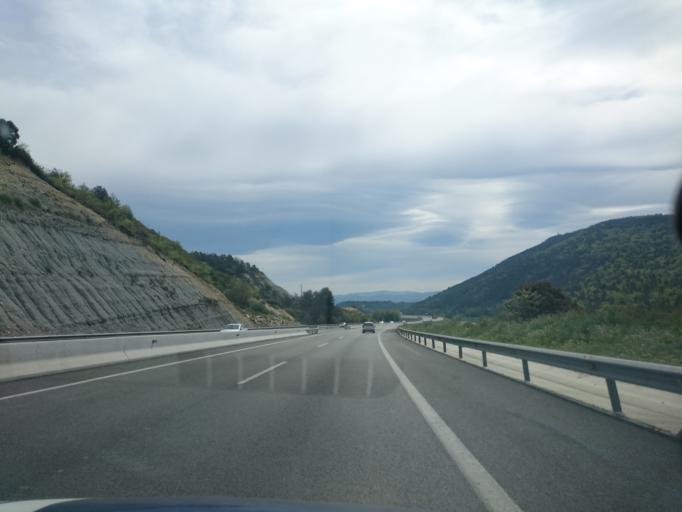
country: ES
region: Catalonia
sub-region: Provincia de Barcelona
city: Muntanyola
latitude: 41.9364
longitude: 2.1815
